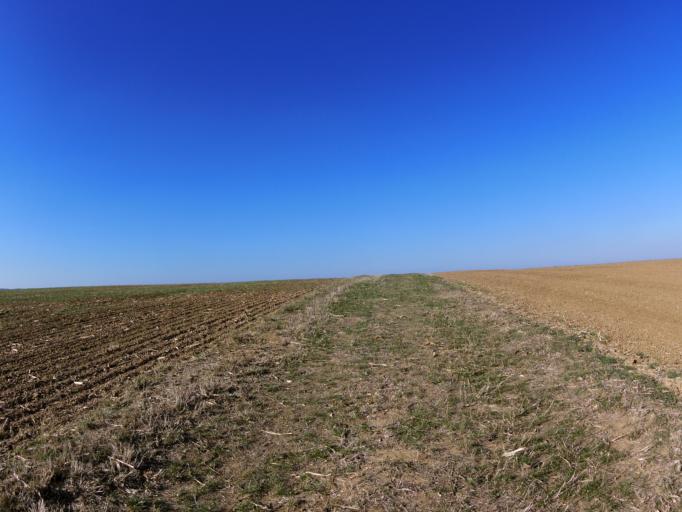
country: DE
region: Bavaria
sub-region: Regierungsbezirk Unterfranken
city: Eibelstadt
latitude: 49.7084
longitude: 9.9764
